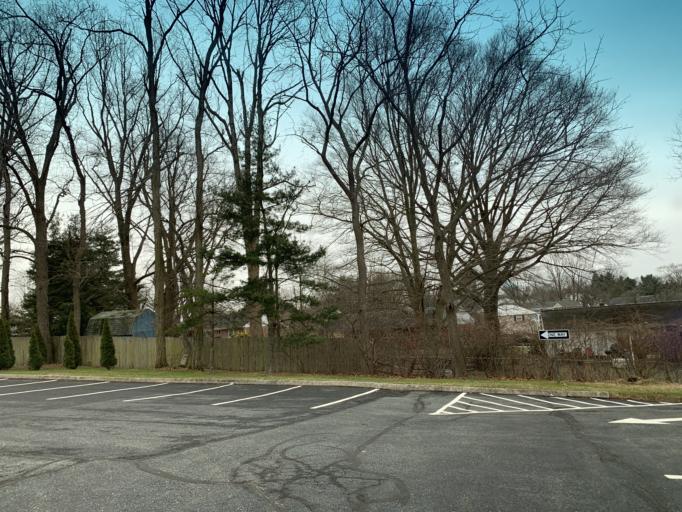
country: US
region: Maryland
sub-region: Harford County
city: South Bel Air
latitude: 39.5472
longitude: -76.3076
